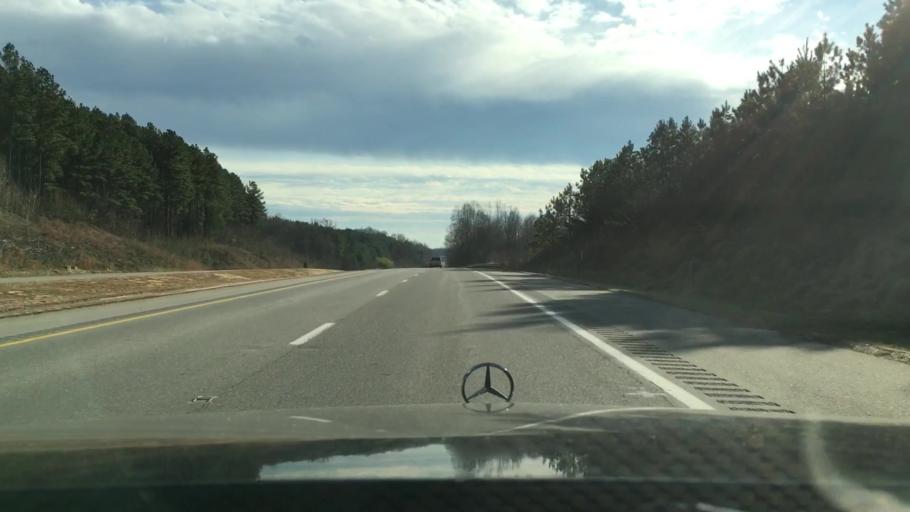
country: US
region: Virginia
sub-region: City of Danville
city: Danville
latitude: 36.6390
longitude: -79.3648
